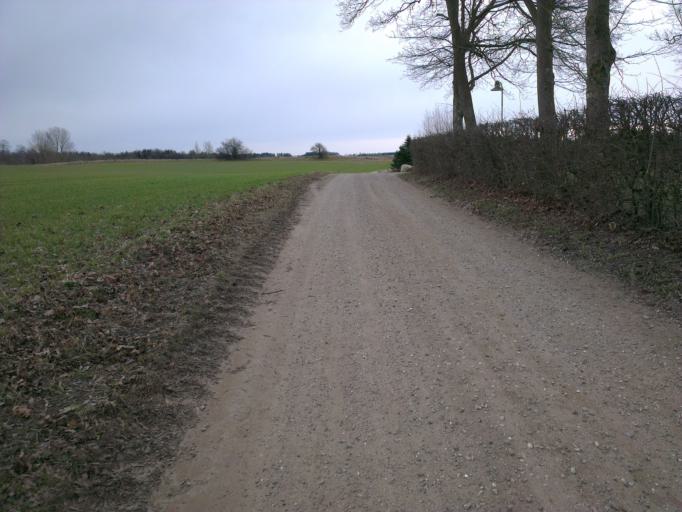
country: DK
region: Zealand
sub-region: Lejre Kommune
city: Ejby
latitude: 55.7666
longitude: 11.8719
